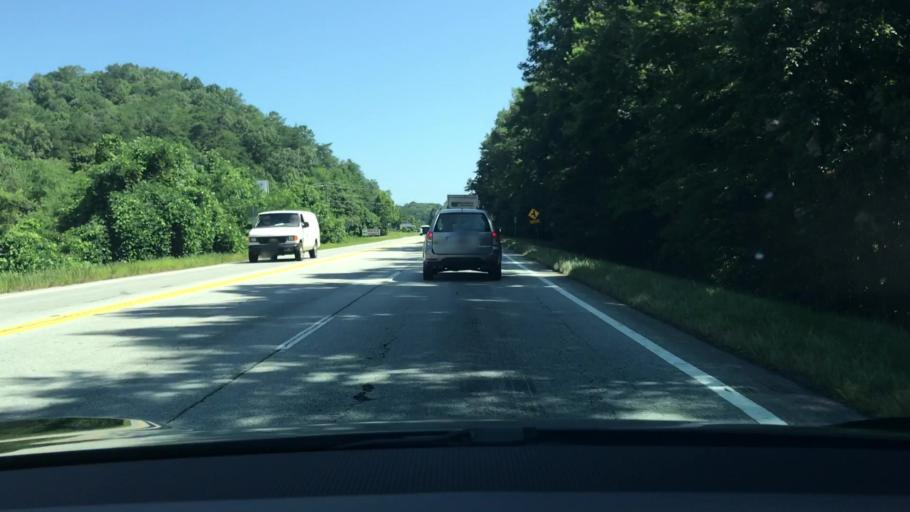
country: US
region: Georgia
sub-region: Rabun County
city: Clayton
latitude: 34.8965
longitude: -83.3929
